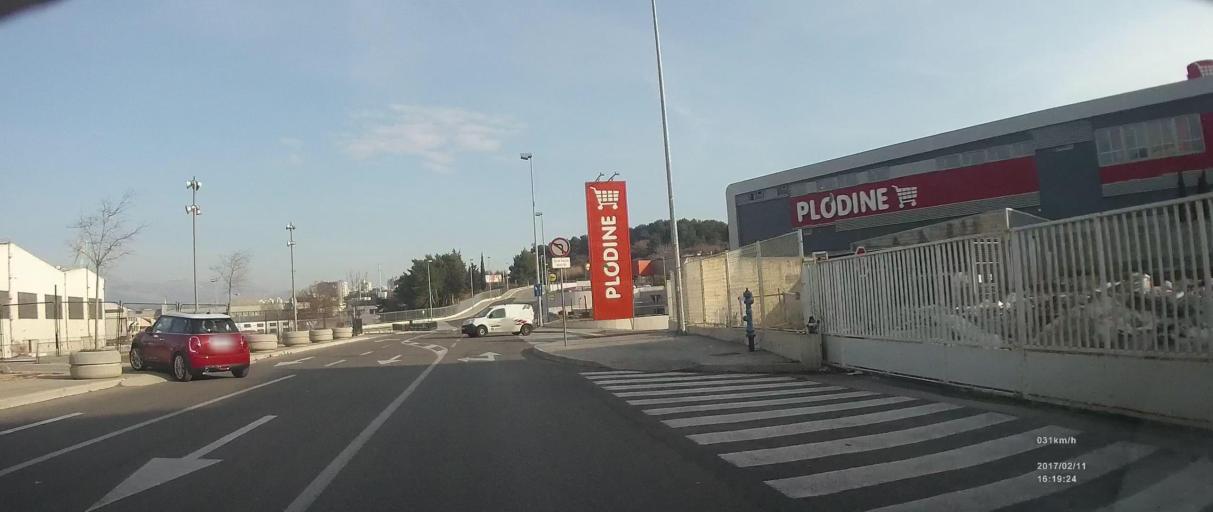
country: HR
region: Splitsko-Dalmatinska
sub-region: Grad Split
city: Split
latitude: 43.5234
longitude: 16.4346
